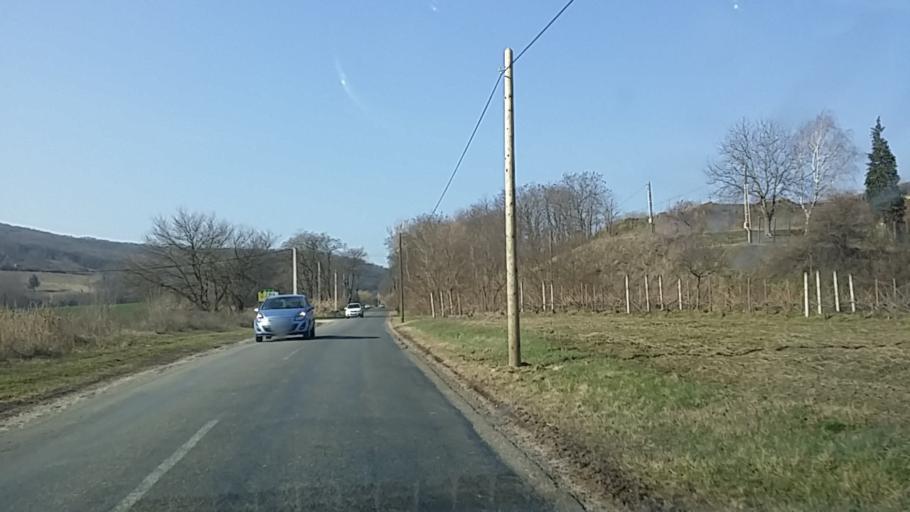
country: HU
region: Komarom-Esztergom
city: Tat
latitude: 47.7326
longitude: 18.6183
